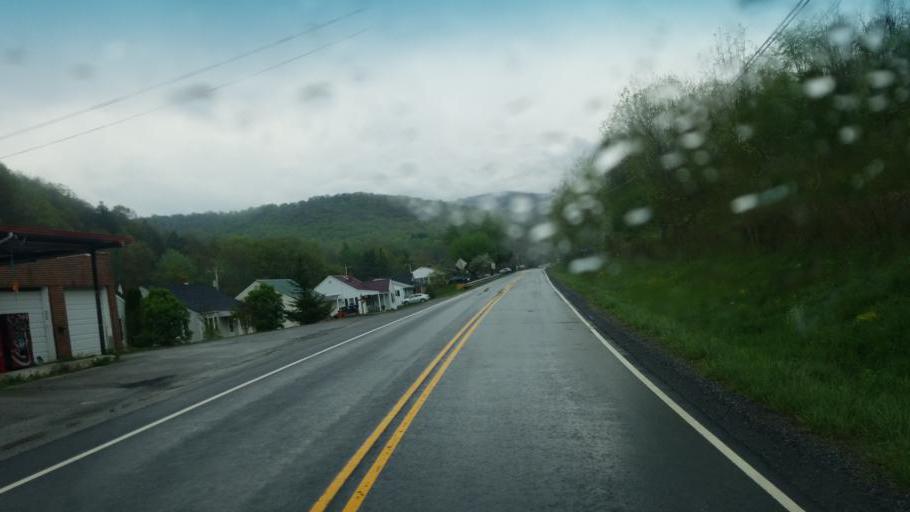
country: US
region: Virginia
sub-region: Smyth County
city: Marion
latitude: 36.8226
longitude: -81.4736
